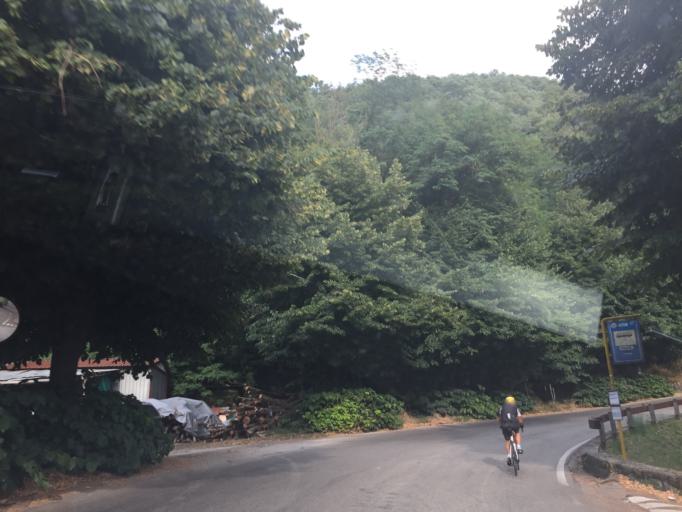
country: IT
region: Tuscany
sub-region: Provincia di Pistoia
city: San Marcello Pistoiese
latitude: 44.0577
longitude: 10.7750
